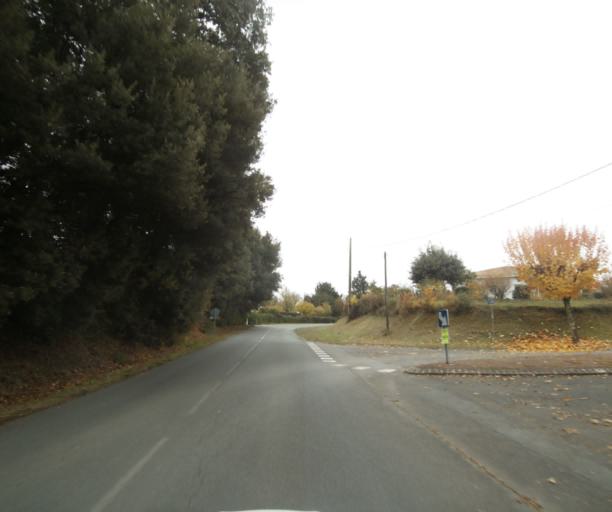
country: FR
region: Poitou-Charentes
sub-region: Departement de la Charente-Maritime
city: Les Gonds
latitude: 45.7247
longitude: -0.6346
